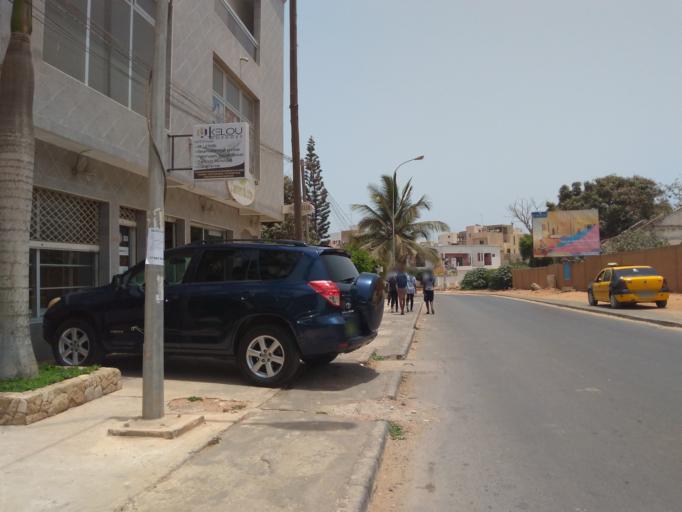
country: SN
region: Dakar
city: Grand Dakar
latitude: 14.7320
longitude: -17.4705
